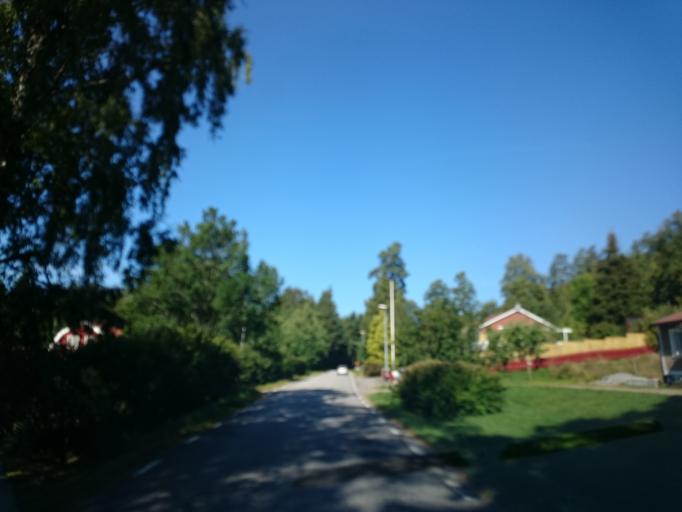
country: SE
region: Soedermanland
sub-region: Nykopings Kommun
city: Olstorp
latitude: 58.6475
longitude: 16.6253
